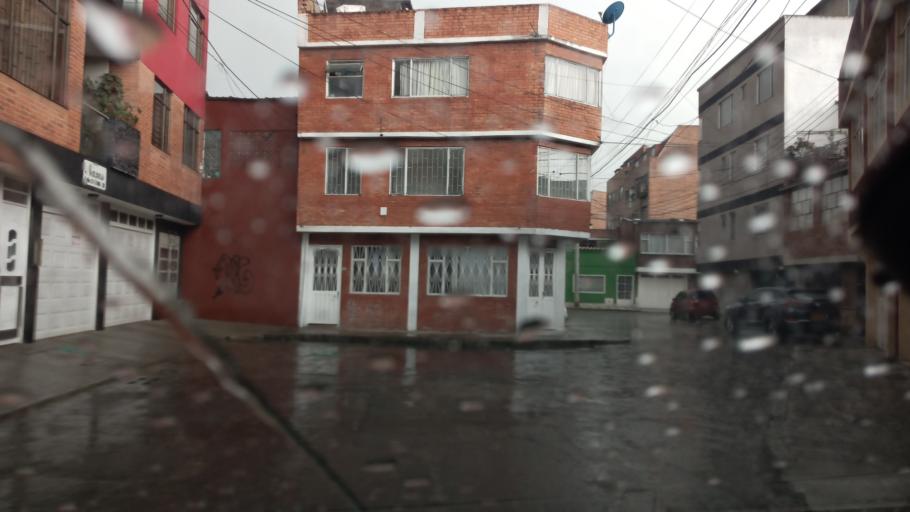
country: CO
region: Bogota D.C.
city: Bogota
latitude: 4.6728
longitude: -74.1384
